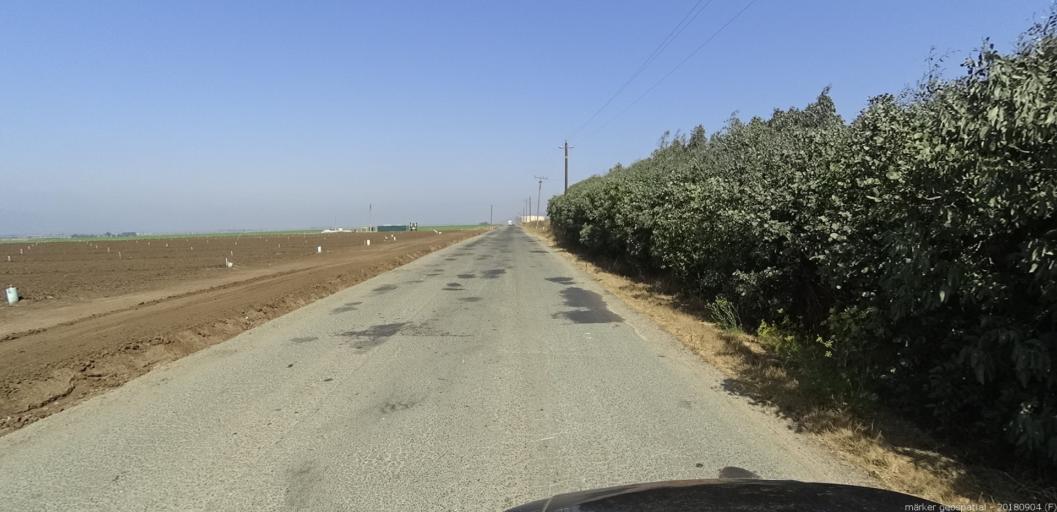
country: US
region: California
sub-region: Monterey County
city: Gonzales
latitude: 36.5194
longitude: -121.4128
